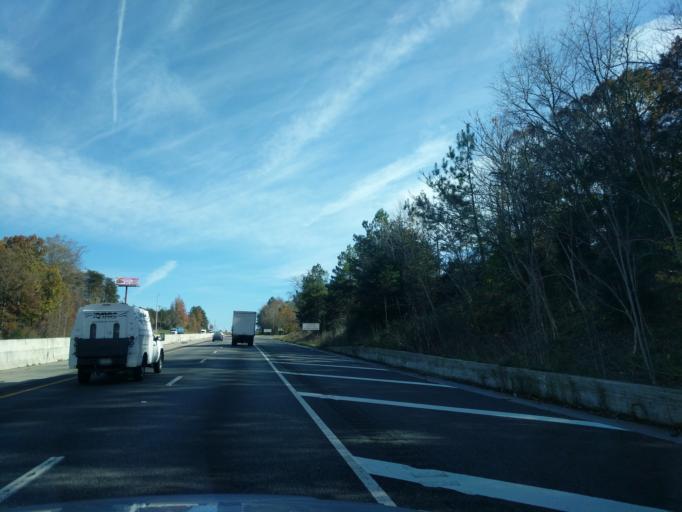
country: US
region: South Carolina
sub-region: Cherokee County
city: Gaffney
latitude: 35.0774
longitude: -81.7238
